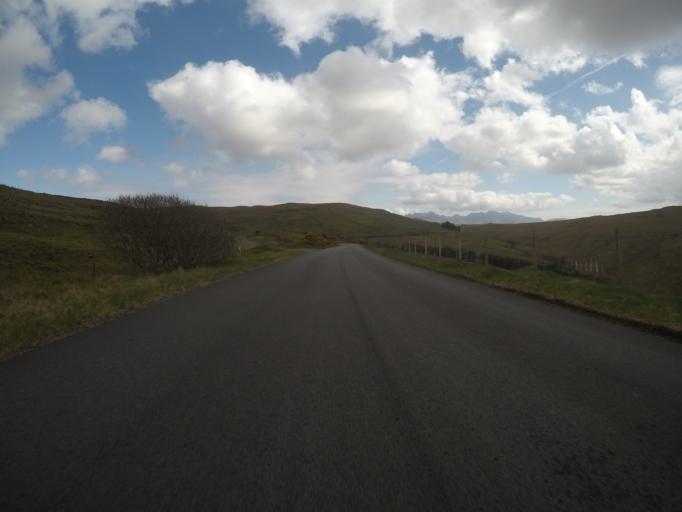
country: GB
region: Scotland
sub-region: Highland
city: Isle of Skye
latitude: 57.3303
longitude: -6.3391
